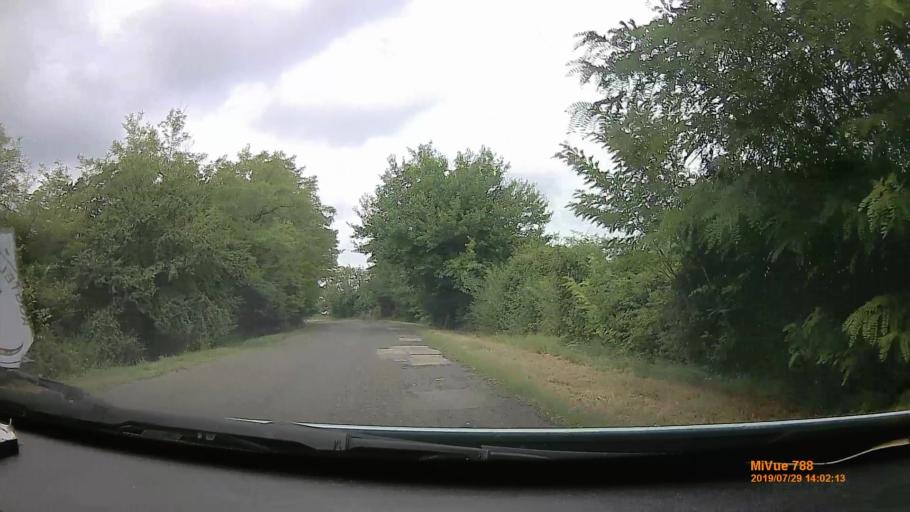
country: HU
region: Somogy
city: Balatonfoldvar
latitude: 46.8029
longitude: 17.9339
